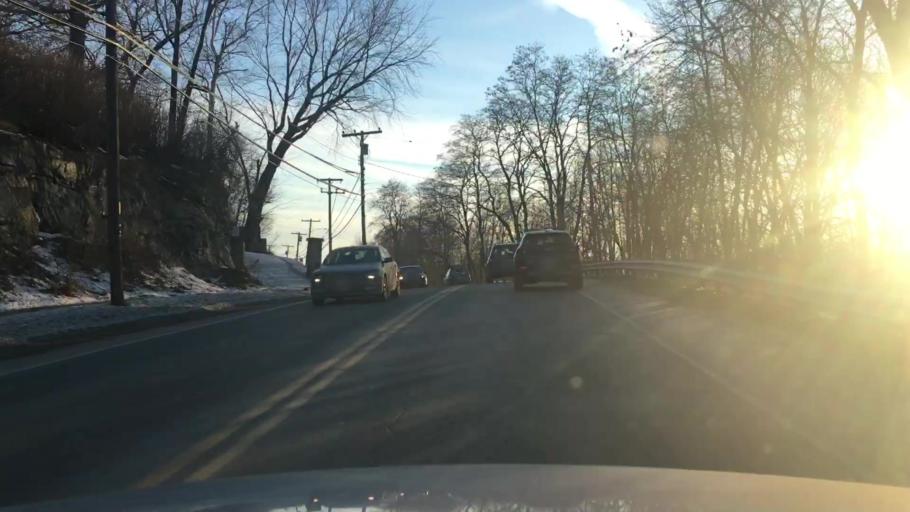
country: US
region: Maine
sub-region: Penobscot County
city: Brewer
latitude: 44.7889
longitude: -68.7702
